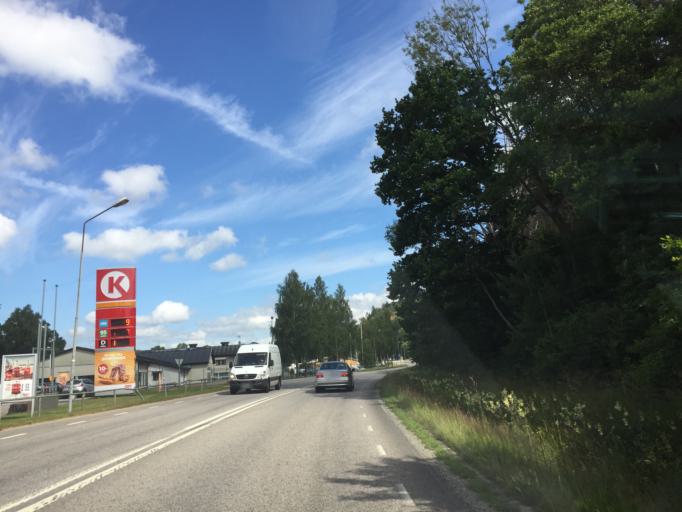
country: SE
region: Vaestra Goetaland
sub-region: Orust
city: Henan
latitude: 58.2324
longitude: 11.6822
